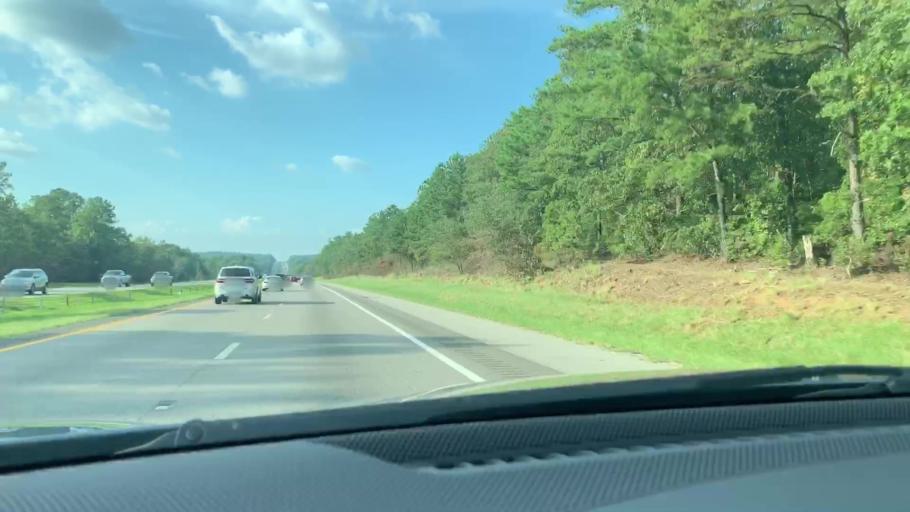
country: US
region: South Carolina
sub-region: Calhoun County
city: Oak Grove
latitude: 33.7122
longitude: -80.9209
